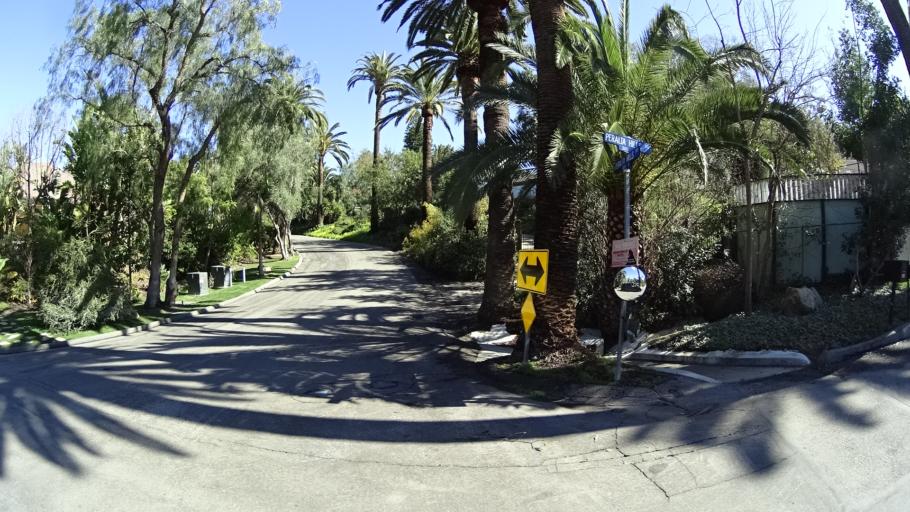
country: US
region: California
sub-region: Orange County
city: Villa Park
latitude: 33.8433
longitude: -117.8232
